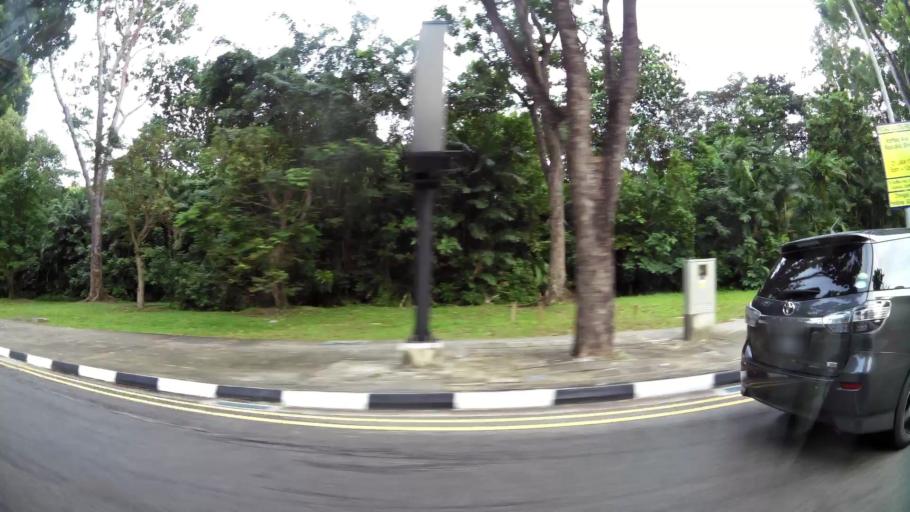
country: SG
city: Singapore
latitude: 1.2981
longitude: 103.8626
